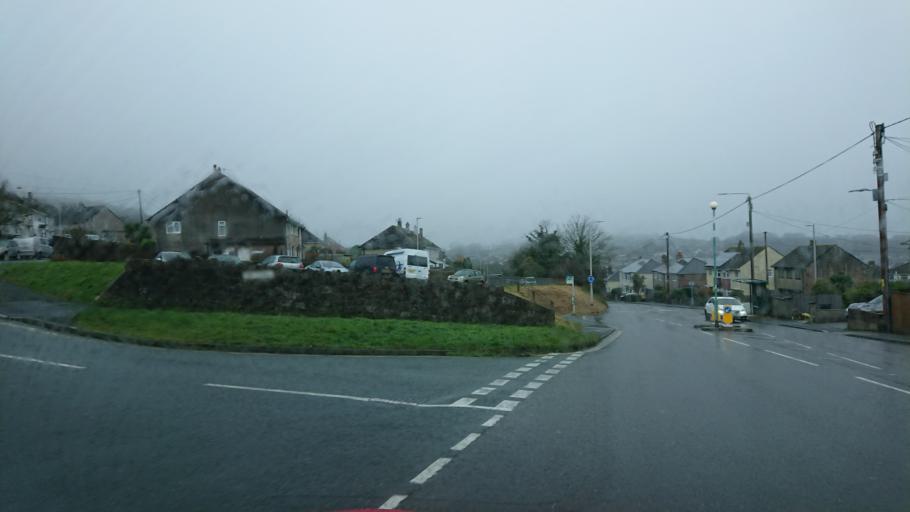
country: GB
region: England
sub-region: Plymouth
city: Plymstock
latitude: 50.3521
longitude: -4.1068
